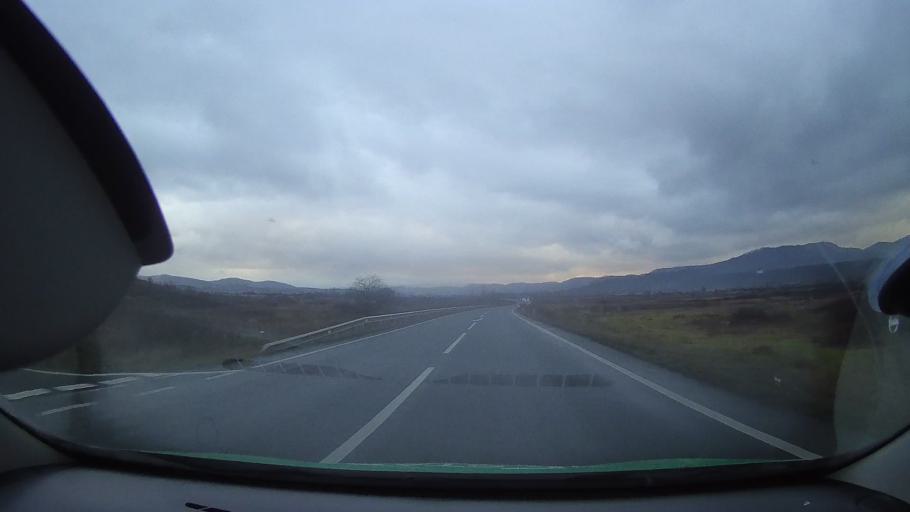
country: RO
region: Hunedoara
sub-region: Comuna Ribita
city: Ribita
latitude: 46.1664
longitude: 22.7496
